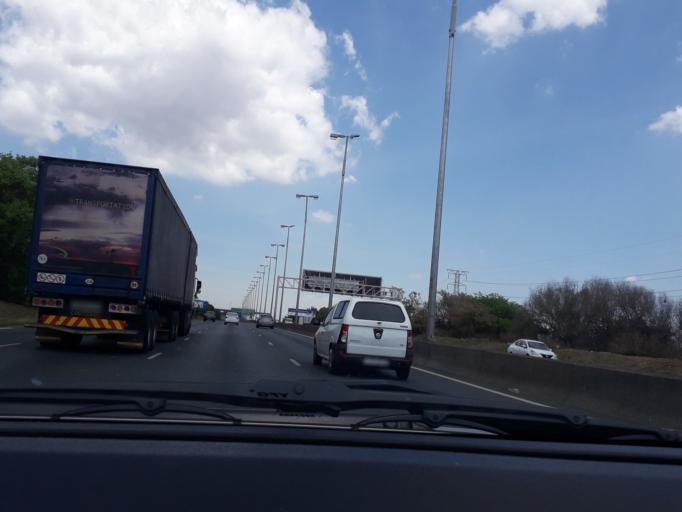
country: ZA
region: Gauteng
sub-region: City of Johannesburg Metropolitan Municipality
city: Johannesburg
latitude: -26.2467
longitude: 28.0036
